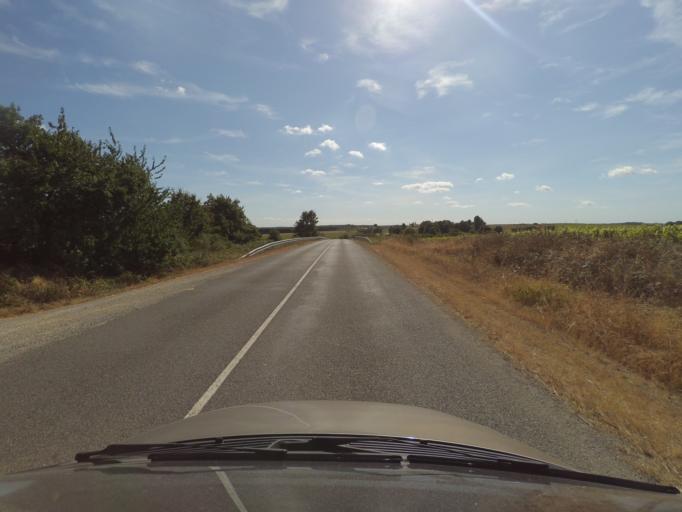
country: FR
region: Pays de la Loire
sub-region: Departement de la Loire-Atlantique
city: Le Bignon
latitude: 47.0887
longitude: -1.4552
